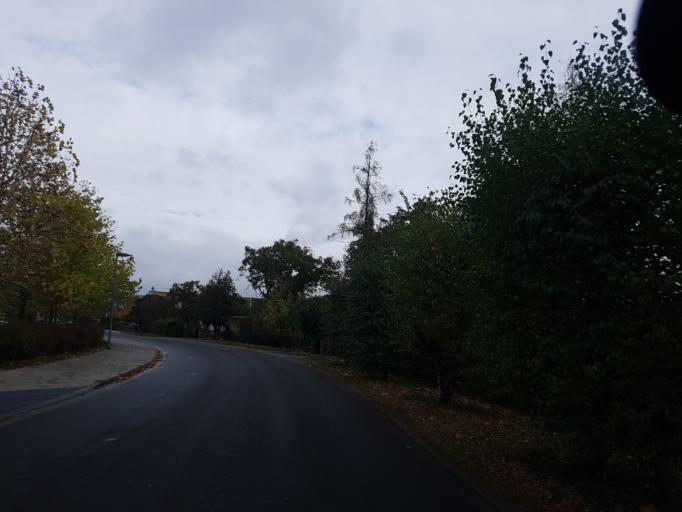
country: DE
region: Brandenburg
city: Herzberg
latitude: 51.6956
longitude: 13.2391
